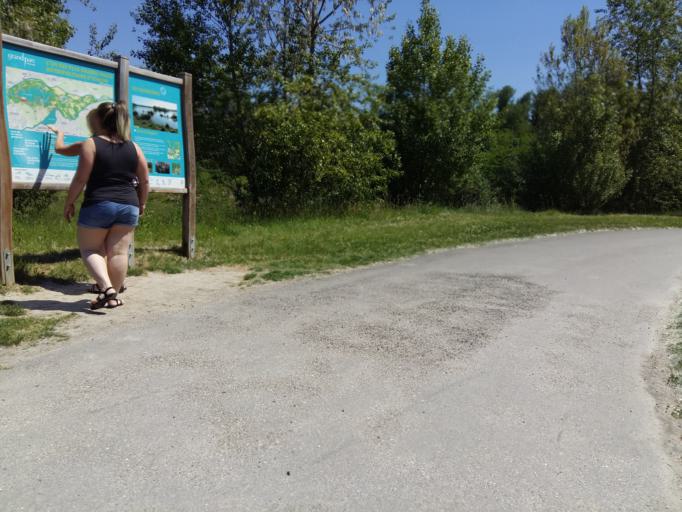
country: FR
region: Rhone-Alpes
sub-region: Departement du Rhone
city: Decines-Charpieu
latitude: 45.7977
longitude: 4.9702
